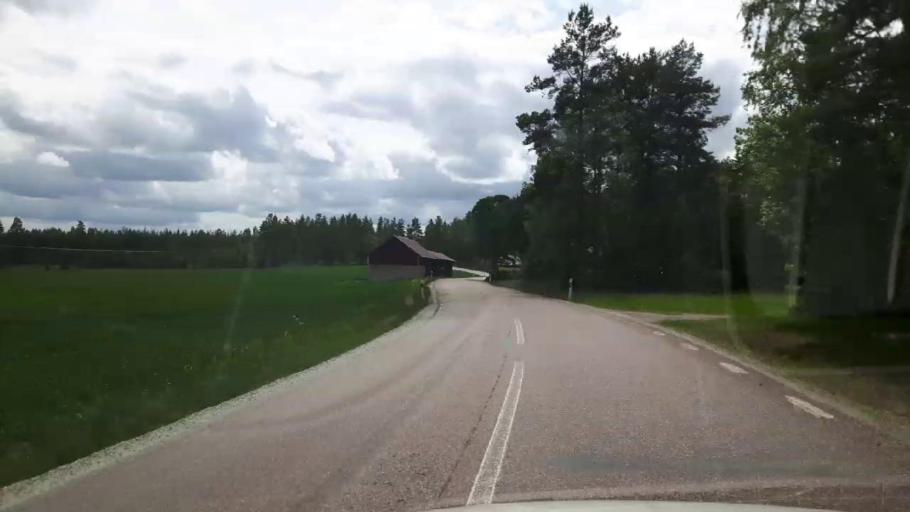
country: SE
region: Vaestmanland
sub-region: Fagersta Kommun
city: Fagersta
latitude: 59.9139
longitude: 15.8248
